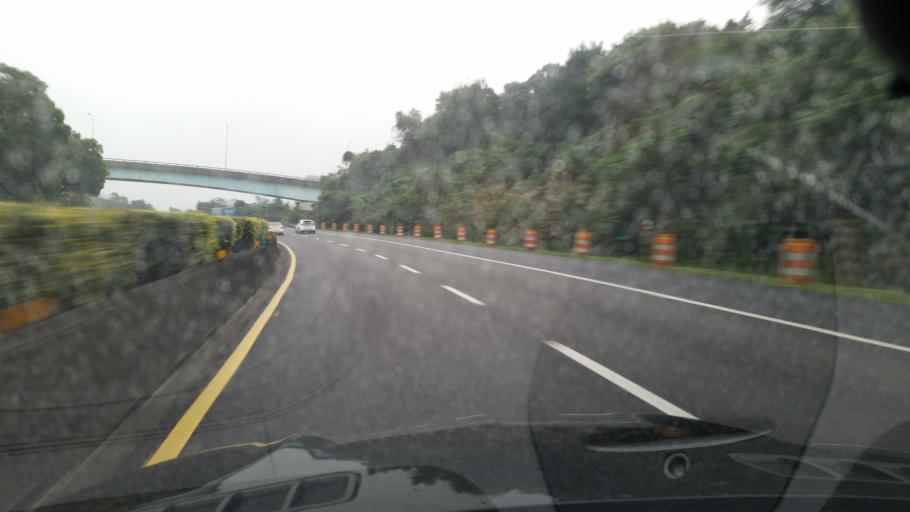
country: TW
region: Taiwan
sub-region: Keelung
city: Keelung
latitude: 25.0974
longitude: 121.7047
